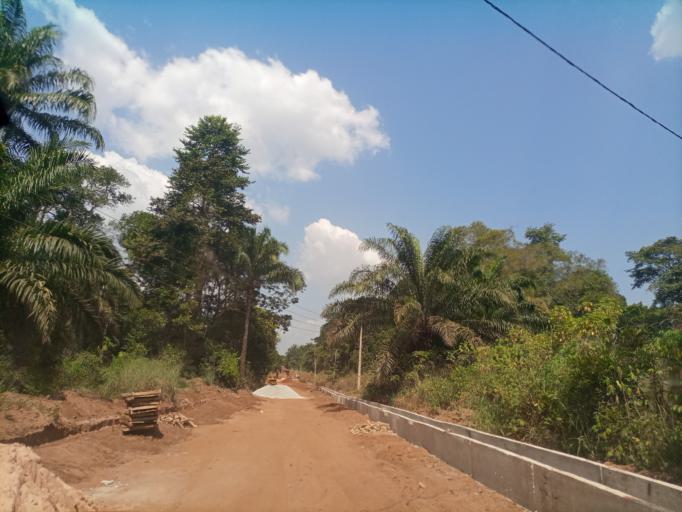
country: NG
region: Enugu
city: Obollo-Afor
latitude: 6.8830
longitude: 7.5200
